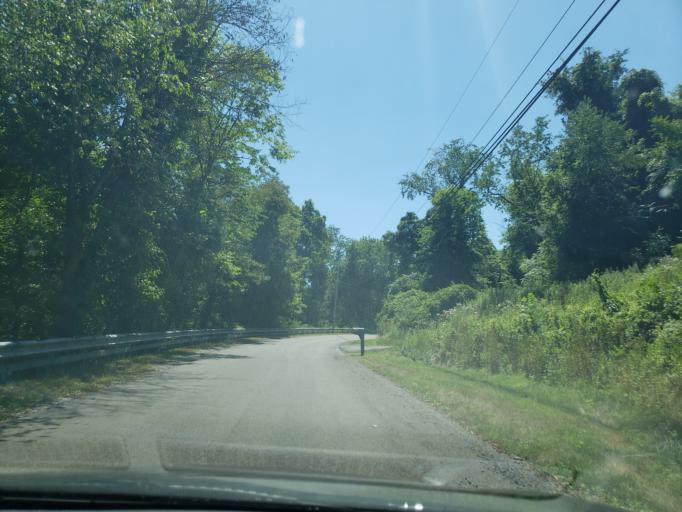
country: US
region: Pennsylvania
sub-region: Allegheny County
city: Emsworth
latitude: 40.5273
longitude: -80.1229
